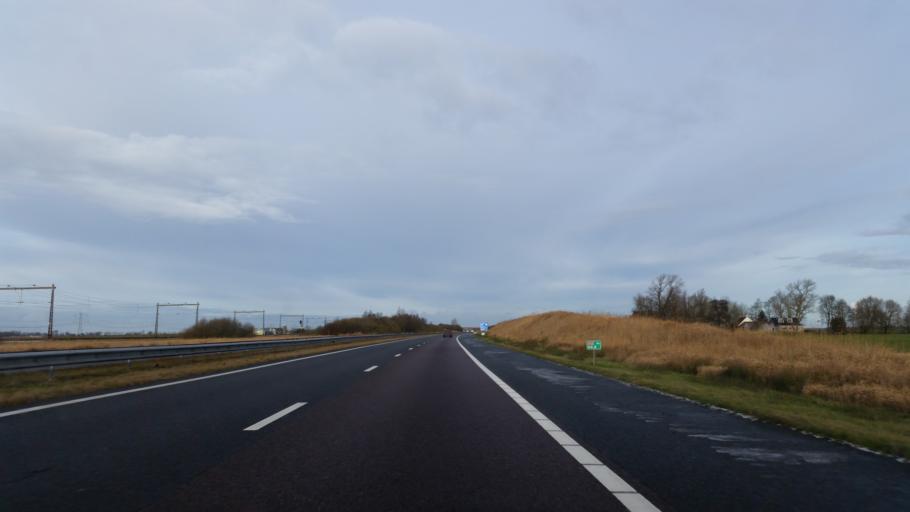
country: NL
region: Friesland
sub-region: Gemeente Boarnsterhim
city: Grou
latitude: 53.1020
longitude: 5.8174
